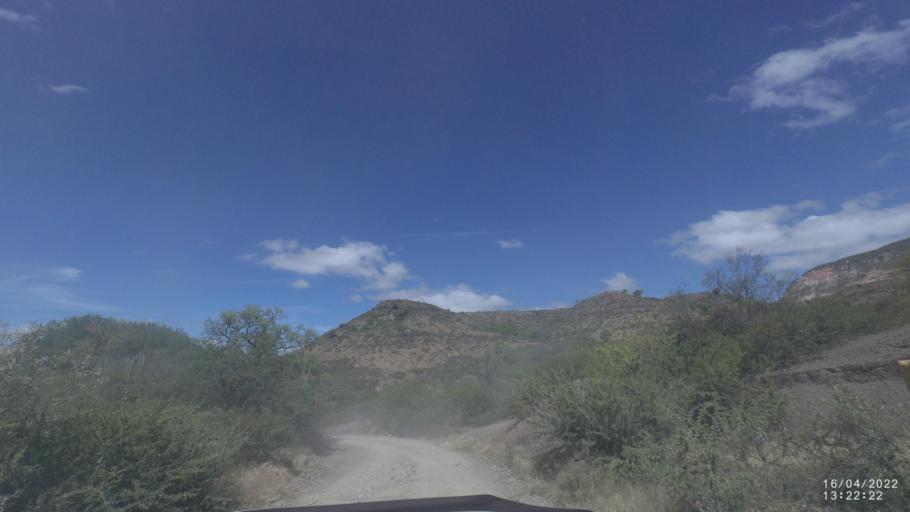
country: BO
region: Cochabamba
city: Mizque
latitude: -17.9928
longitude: -65.6064
